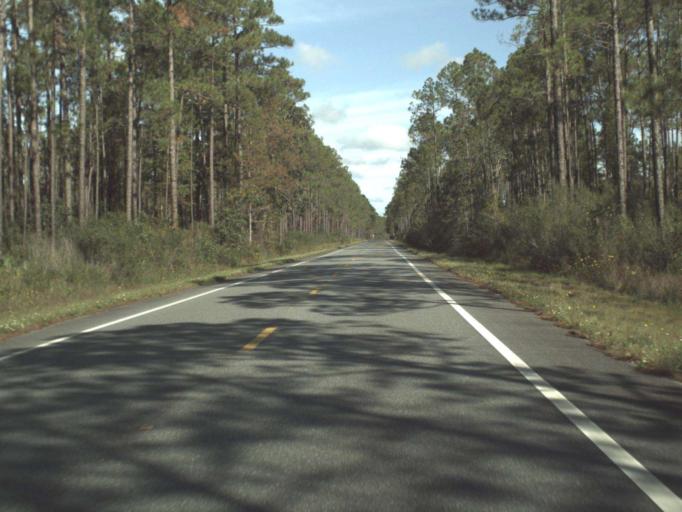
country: US
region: Florida
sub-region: Franklin County
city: Apalachicola
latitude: 29.9550
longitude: -84.9762
